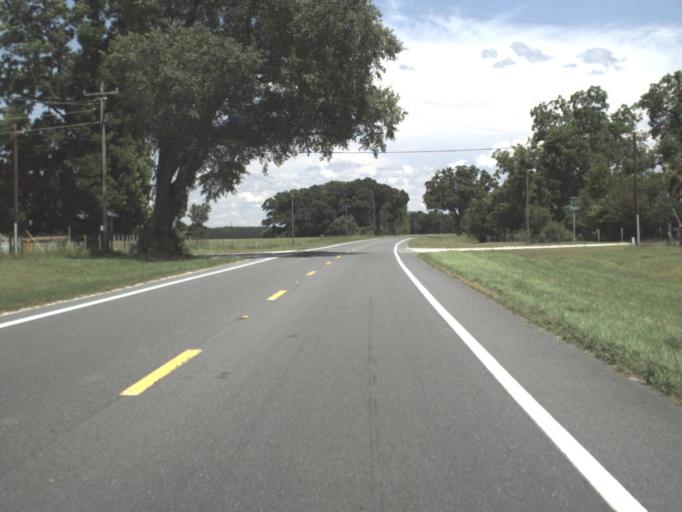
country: US
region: Florida
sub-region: Lafayette County
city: Mayo
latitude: 30.1269
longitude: -83.2758
